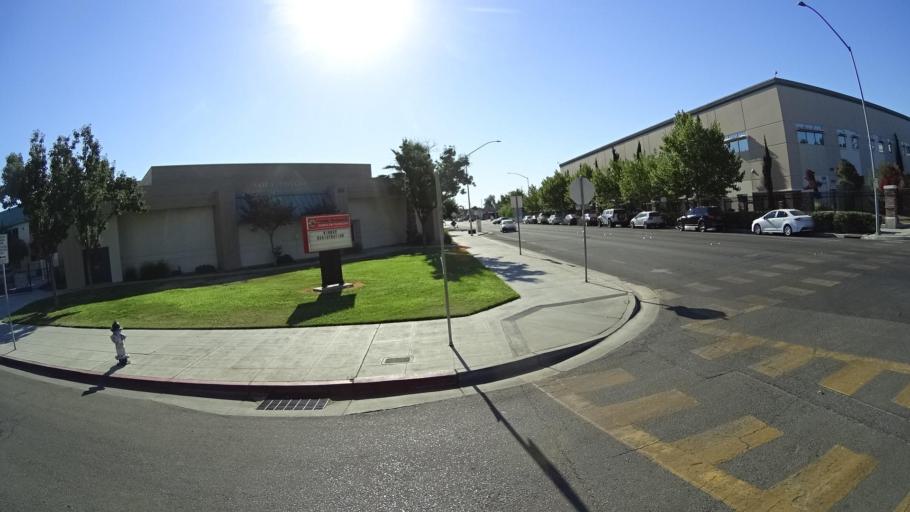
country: US
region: California
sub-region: Fresno County
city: Fresno
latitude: 36.7470
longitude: -119.7839
